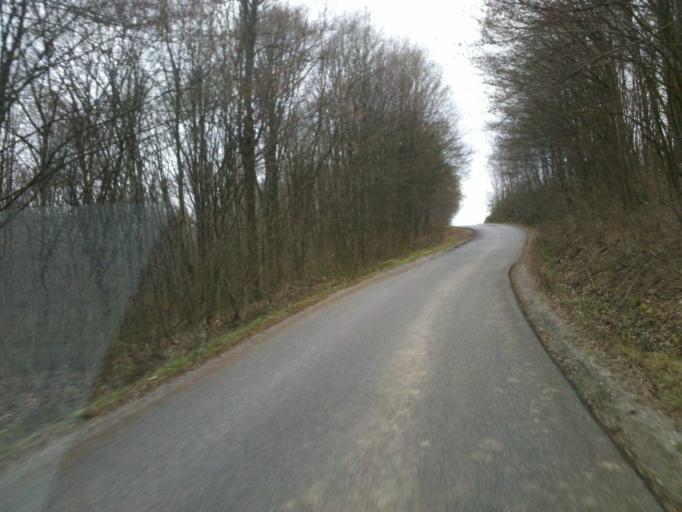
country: HR
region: Grad Zagreb
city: Horvati
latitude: 45.6690
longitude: 15.8230
